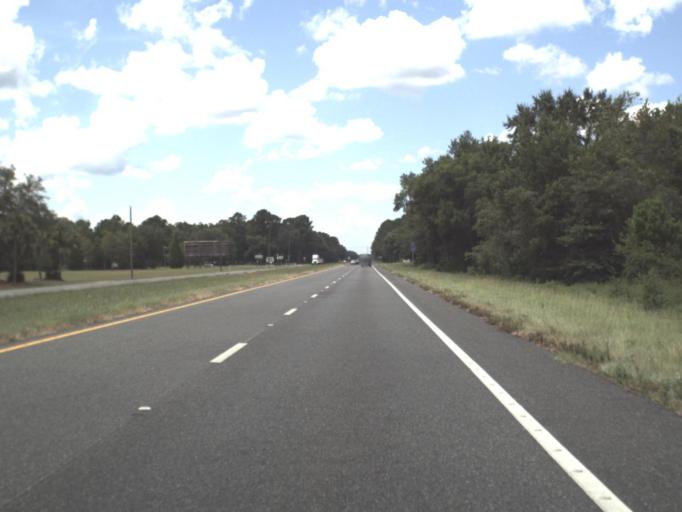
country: US
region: Florida
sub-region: Taylor County
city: Perry
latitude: 30.1617
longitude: -83.6234
